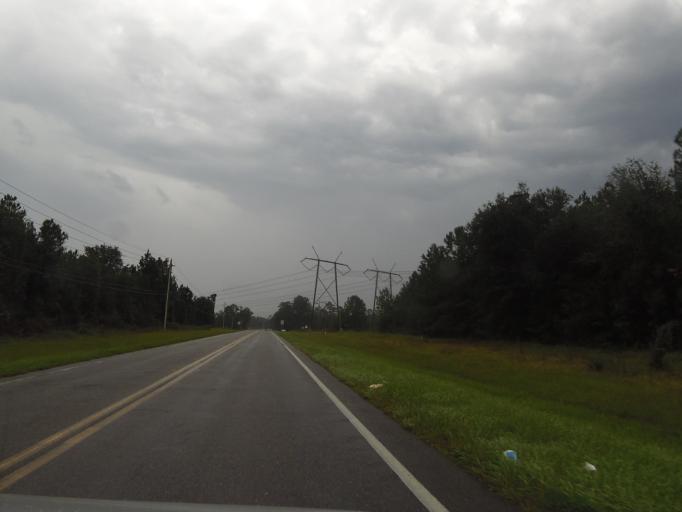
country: US
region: Florida
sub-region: Clay County
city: Middleburg
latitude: 30.0893
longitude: -81.8418
